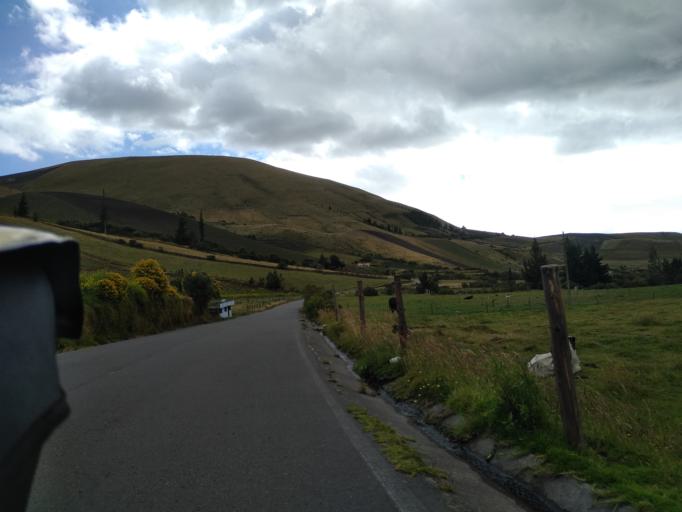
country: EC
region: Cotopaxi
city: Saquisili
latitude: -0.7262
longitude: -78.7568
